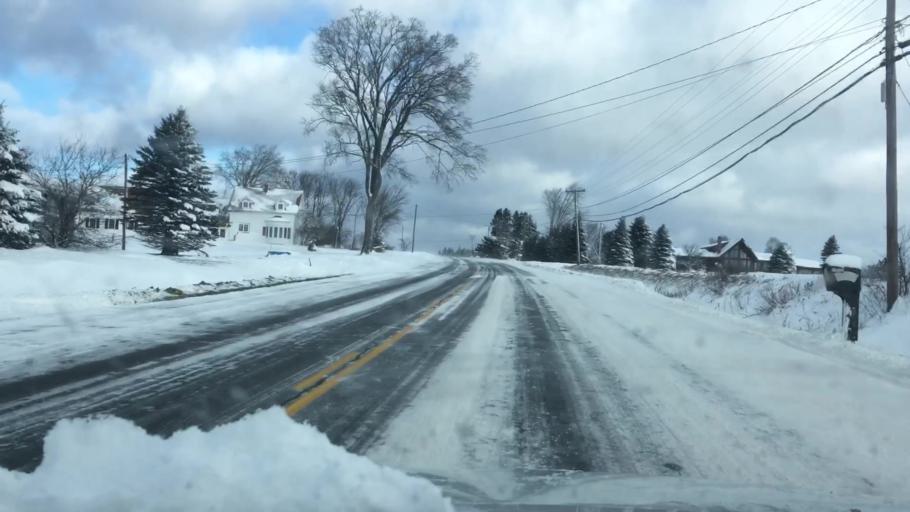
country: US
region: Maine
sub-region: Aroostook County
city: Caribou
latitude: 46.9010
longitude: -68.0153
